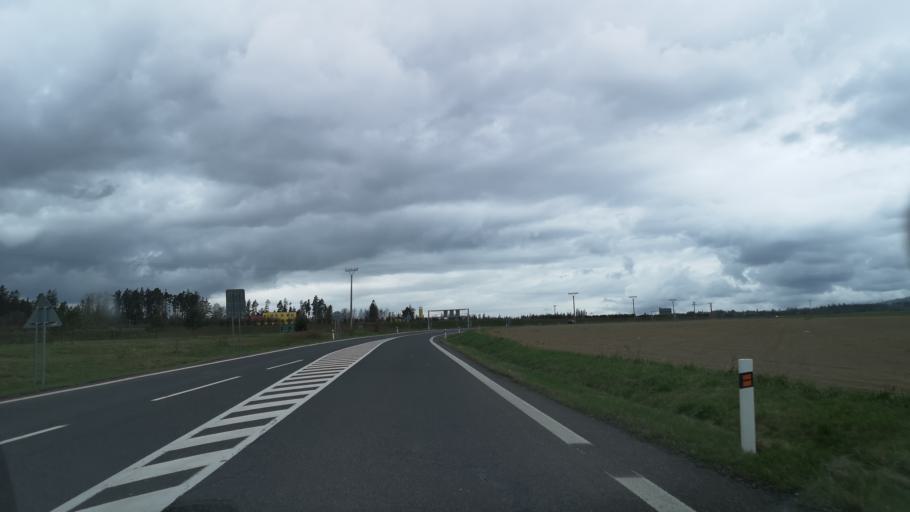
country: SK
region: Presovsky
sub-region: Okres Poprad
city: Strba
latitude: 49.0665
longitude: 20.1392
